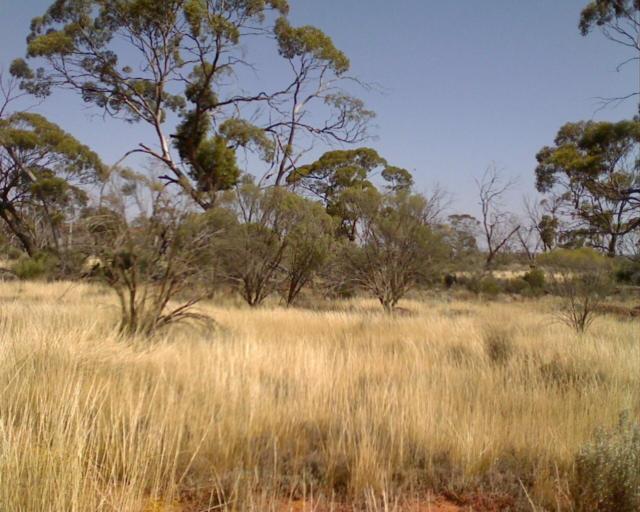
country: AU
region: Western Australia
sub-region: Merredin
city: Merredin
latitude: -30.9619
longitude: 118.8891
